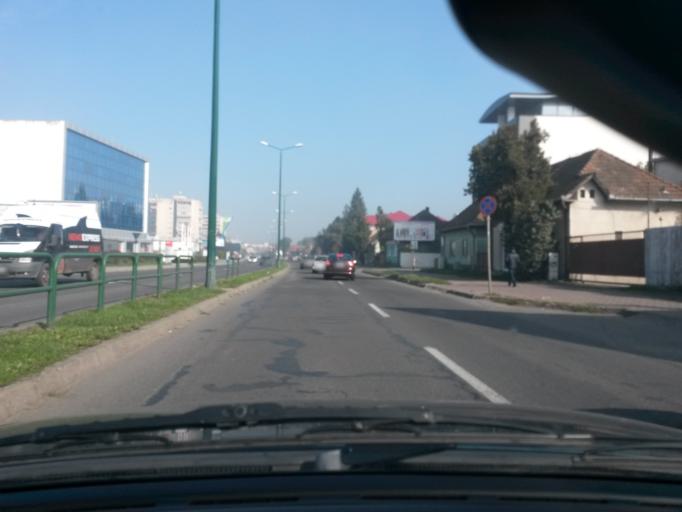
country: RO
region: Mures
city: Targu-Mures
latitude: 46.5298
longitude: 24.5480
